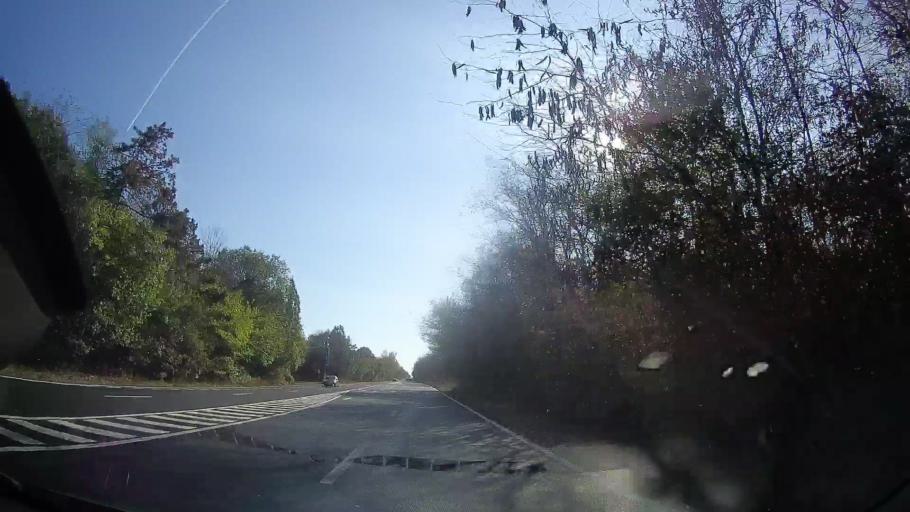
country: RO
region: Constanta
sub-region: Comuna Douazeci si Trei August
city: Dulcesti
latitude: 43.8759
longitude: 28.5739
